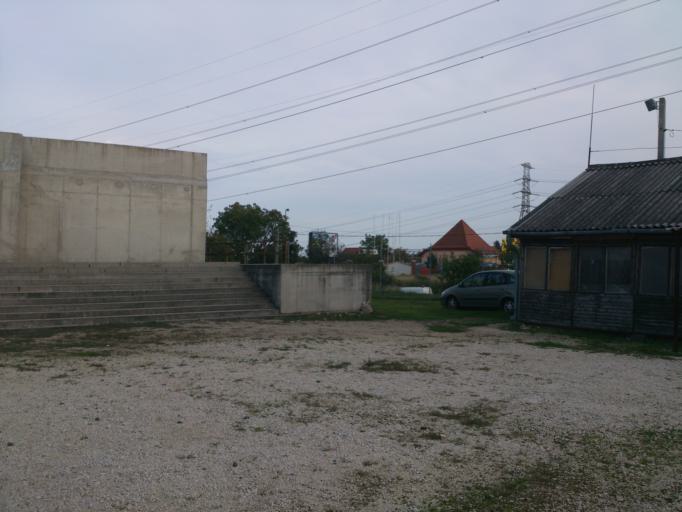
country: HU
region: Budapest
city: Budapest XXII. keruelet
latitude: 47.4266
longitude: 19.0003
